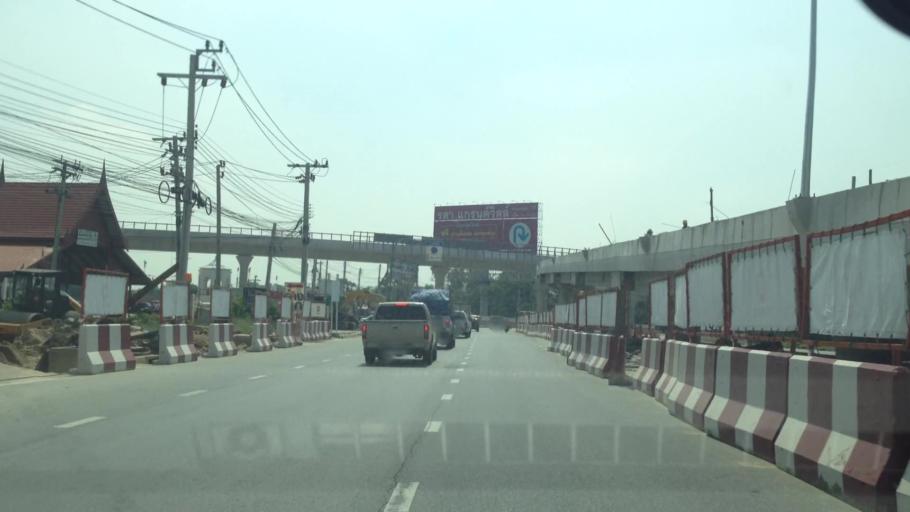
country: TH
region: Bangkok
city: Sai Mai
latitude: 13.9282
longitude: 100.6265
